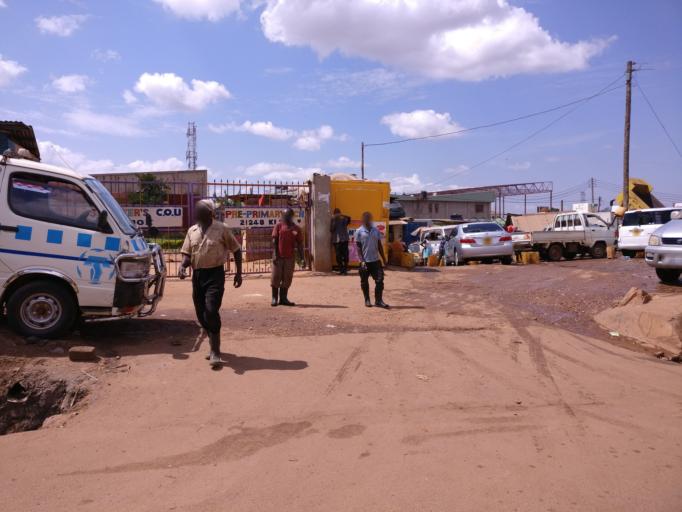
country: UG
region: Central Region
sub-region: Kampala District
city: Kampala
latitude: 0.2951
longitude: 32.5647
